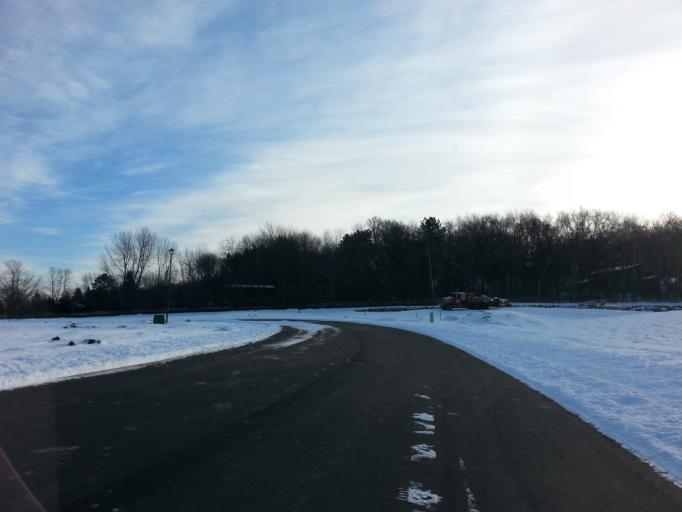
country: US
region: Minnesota
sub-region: Scott County
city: Prior Lake
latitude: 44.7631
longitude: -93.4155
